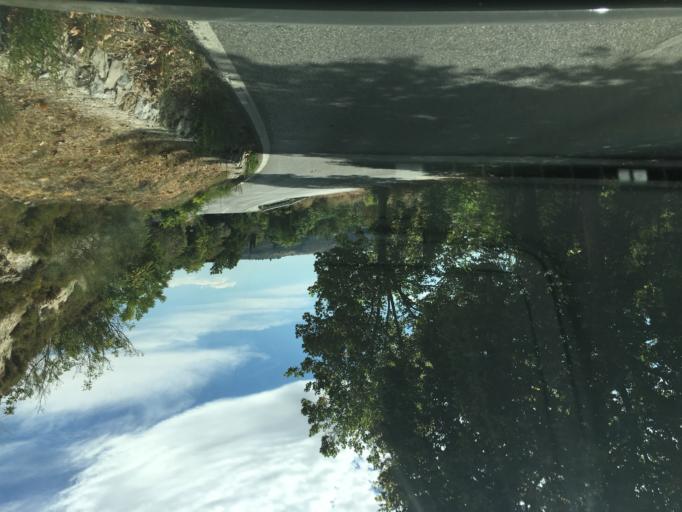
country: ES
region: Andalusia
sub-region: Provincia de Granada
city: Huetor Santillan
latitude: 37.2278
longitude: -3.5031
